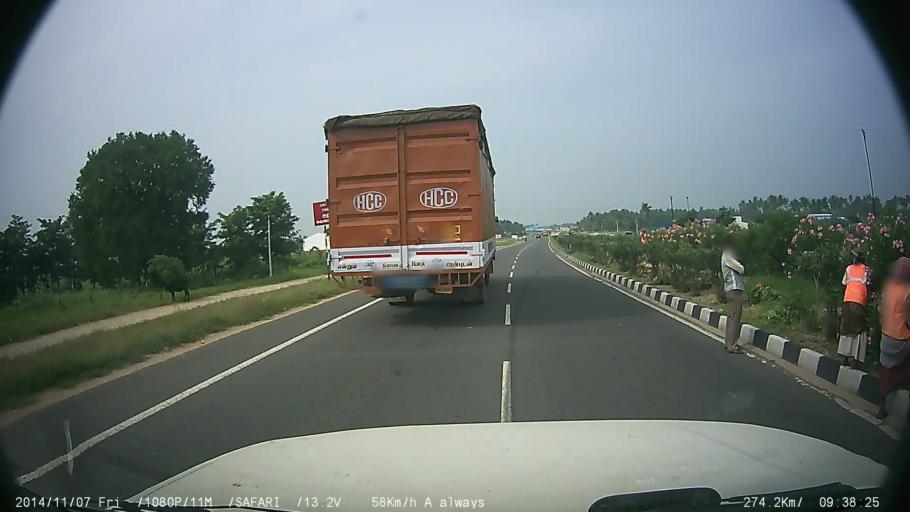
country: IN
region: Tamil Nadu
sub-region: Erode
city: Perundurai
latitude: 11.3439
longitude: 77.6386
